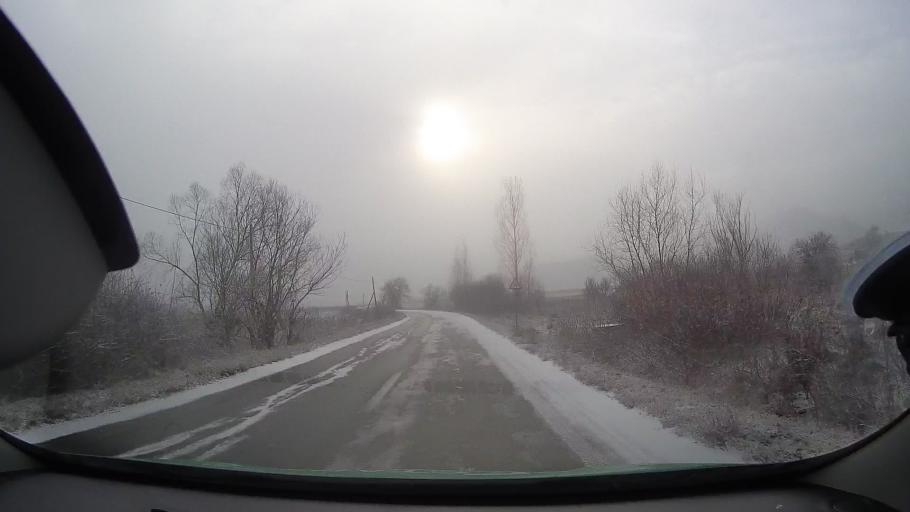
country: RO
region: Alba
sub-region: Comuna Rimetea
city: Rimetea
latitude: 46.4029
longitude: 23.5577
